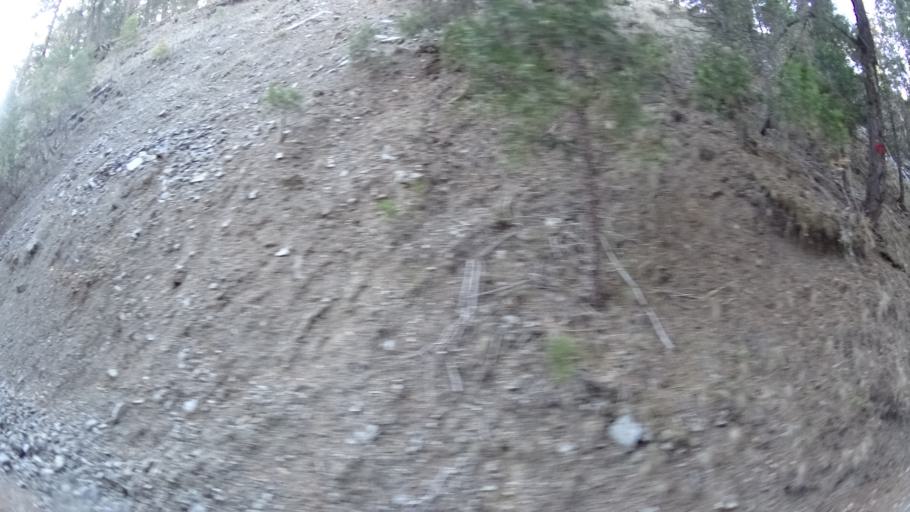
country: US
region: California
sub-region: Siskiyou County
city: Yreka
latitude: 41.8413
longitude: -122.8811
